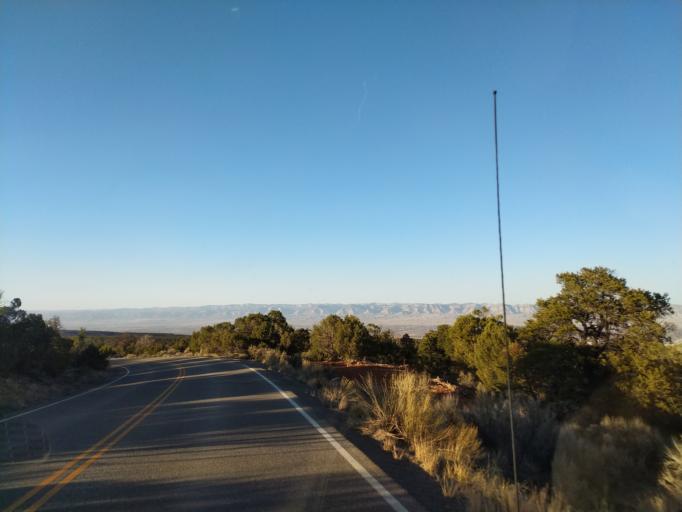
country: US
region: Colorado
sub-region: Mesa County
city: Redlands
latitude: 39.0210
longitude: -108.6595
